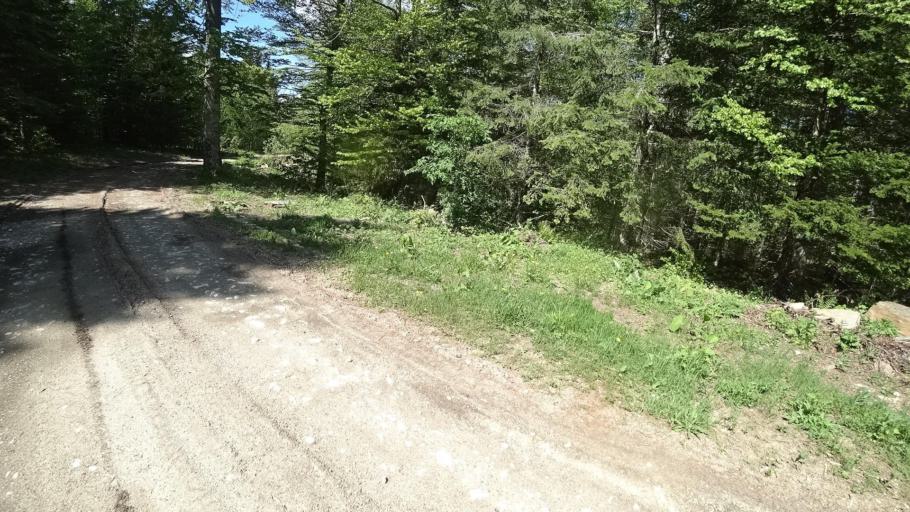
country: BA
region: Federation of Bosnia and Herzegovina
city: Orasac
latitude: 44.7215
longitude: 16.1487
